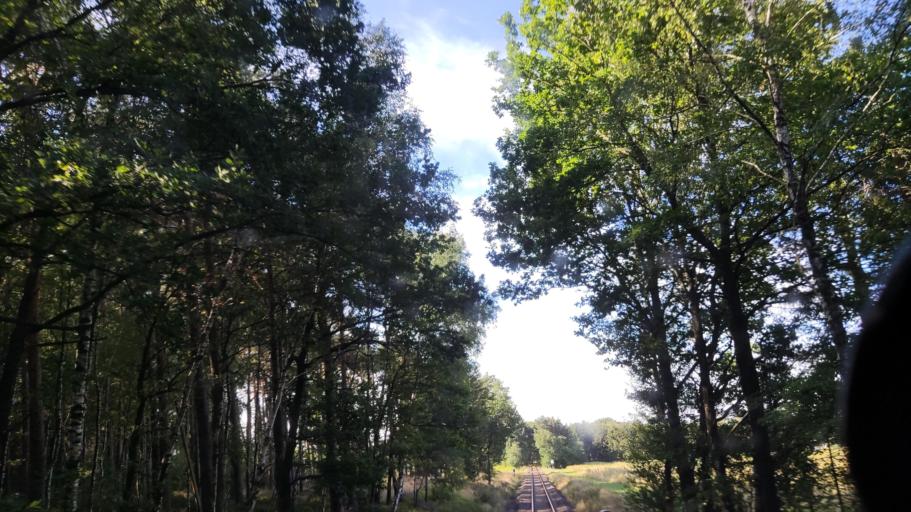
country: DE
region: Lower Saxony
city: Bispingen
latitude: 53.0388
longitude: 9.9372
